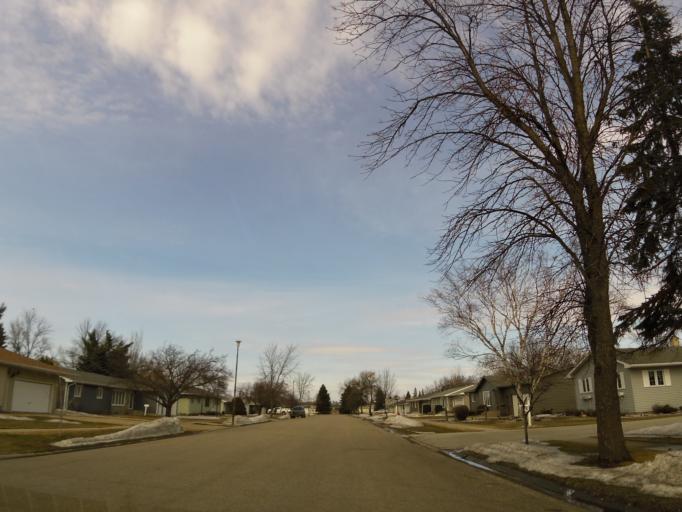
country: US
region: North Dakota
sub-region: Walsh County
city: Grafton
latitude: 48.4091
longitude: -97.4220
